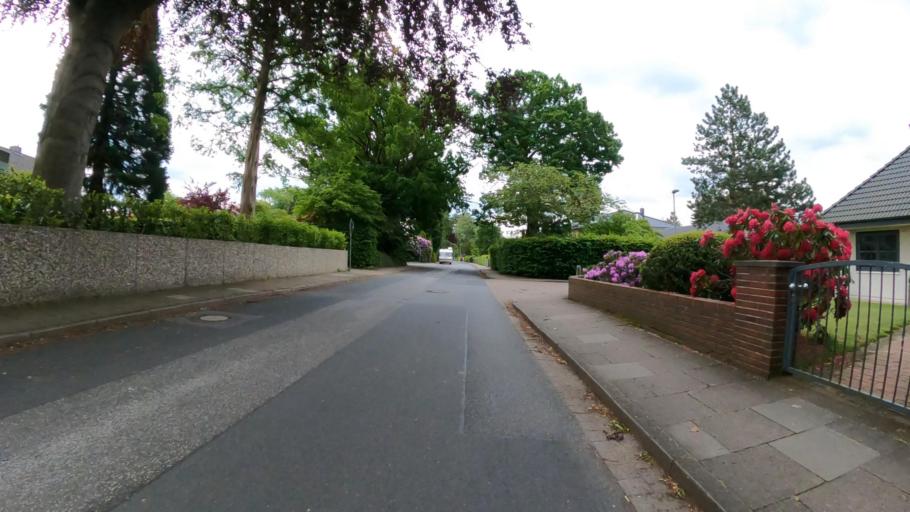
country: DE
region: Schleswig-Holstein
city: Rellingen
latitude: 53.6539
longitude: 9.8166
